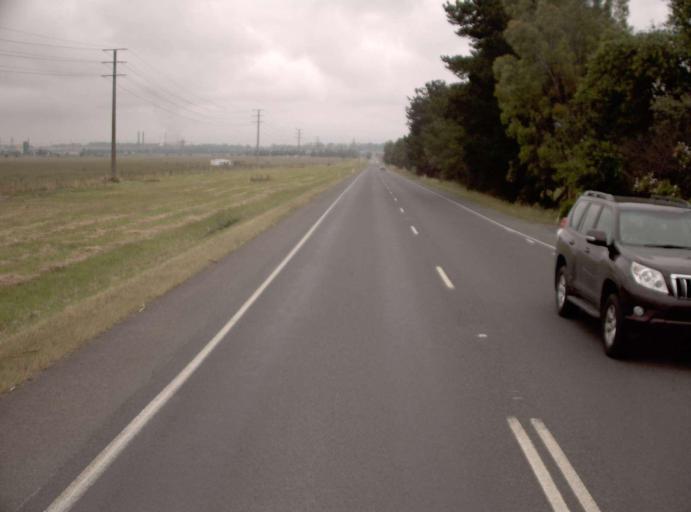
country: AU
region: Victoria
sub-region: Latrobe
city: Morwell
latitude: -38.2513
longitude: 146.4574
